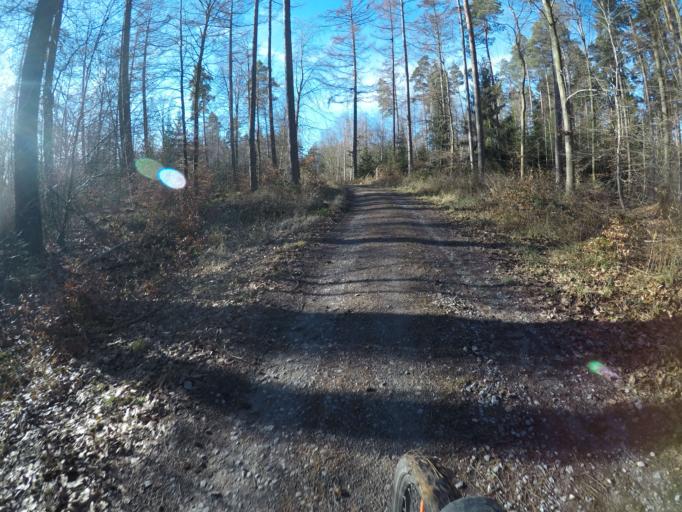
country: DE
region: Baden-Wuerttemberg
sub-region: Regierungsbezirk Stuttgart
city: Steinenbronn
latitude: 48.6929
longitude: 9.1024
